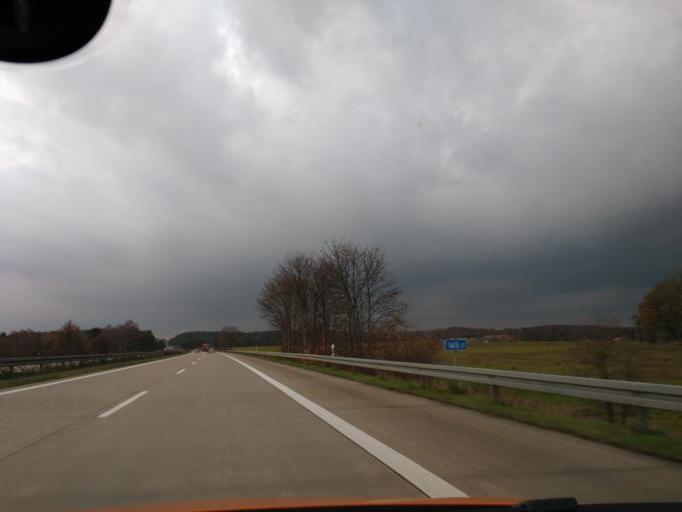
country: DE
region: Brandenburg
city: Heiligengrabe
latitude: 53.1690
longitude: 12.3616
